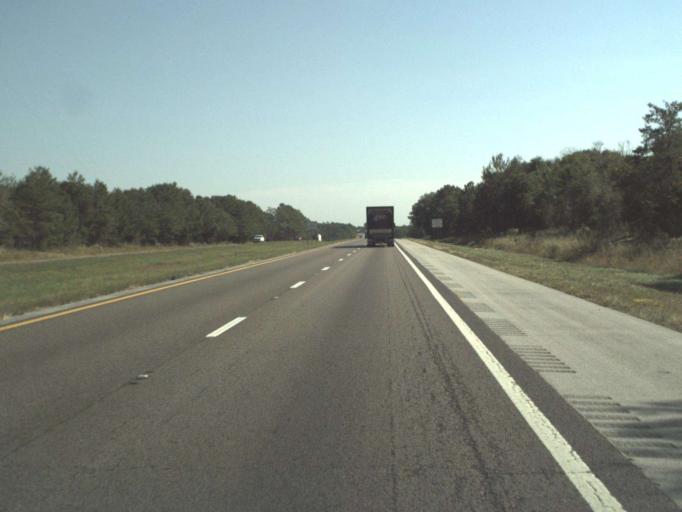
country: US
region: Florida
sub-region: Walton County
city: DeFuniak Springs
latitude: 30.7395
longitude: -86.2263
